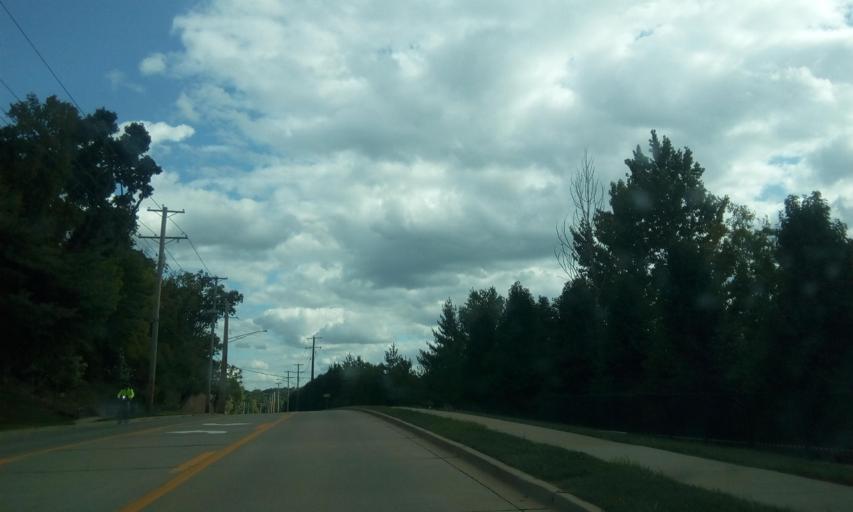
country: US
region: Missouri
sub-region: Saint Louis County
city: Town and Country
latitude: 38.5903
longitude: -90.4709
